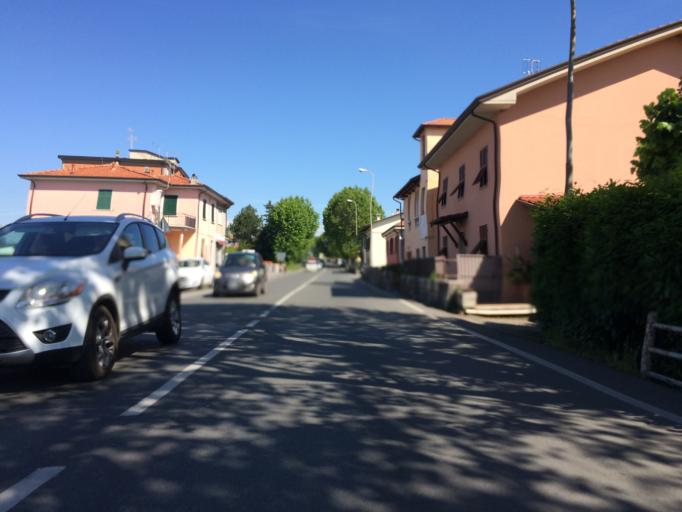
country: IT
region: Liguria
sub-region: Provincia di La Spezia
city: Colombiera-Molicciara
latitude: 44.0789
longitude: 10.0114
